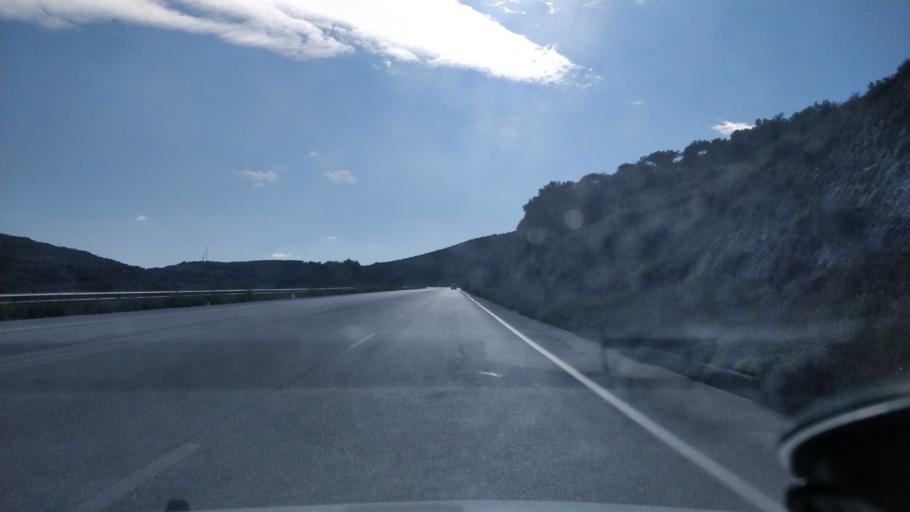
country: GR
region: Crete
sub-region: Nomos Irakleiou
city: Ano Arhanes
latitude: 35.2535
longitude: 25.1784
